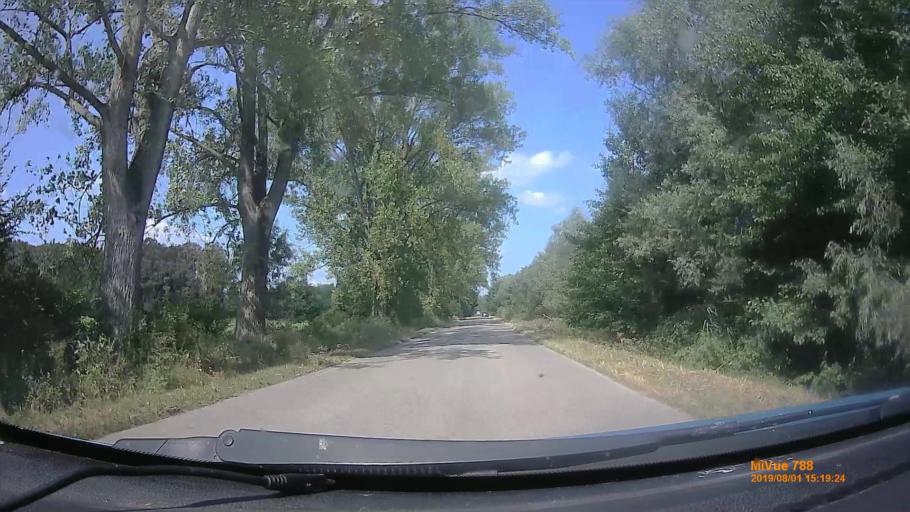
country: HU
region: Baranya
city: Sellye
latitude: 45.8544
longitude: 17.8232
